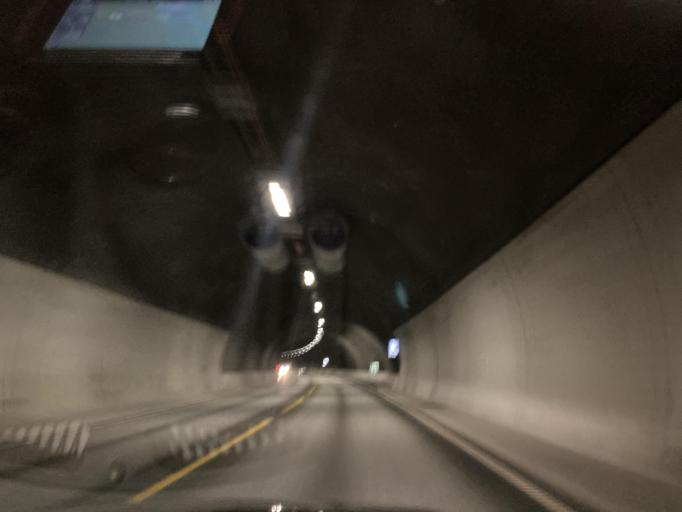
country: NO
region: Hordaland
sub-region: Etne
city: Etne
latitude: 59.7165
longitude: 6.1016
